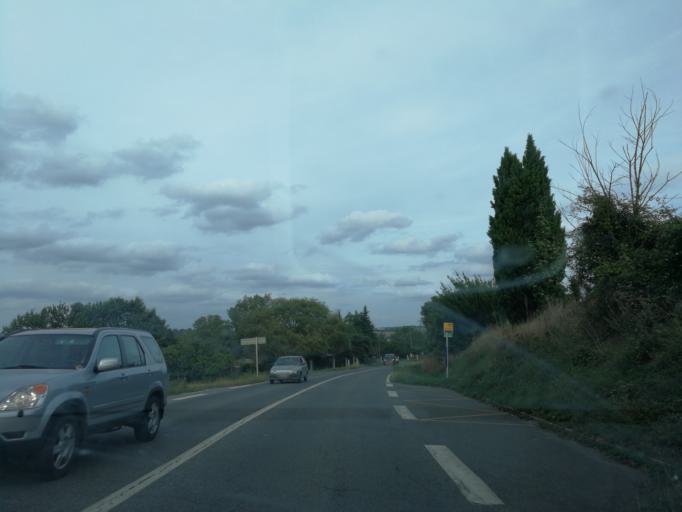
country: FR
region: Midi-Pyrenees
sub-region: Departement de la Haute-Garonne
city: Dremil-Lafage
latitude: 43.5883
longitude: 1.5827
